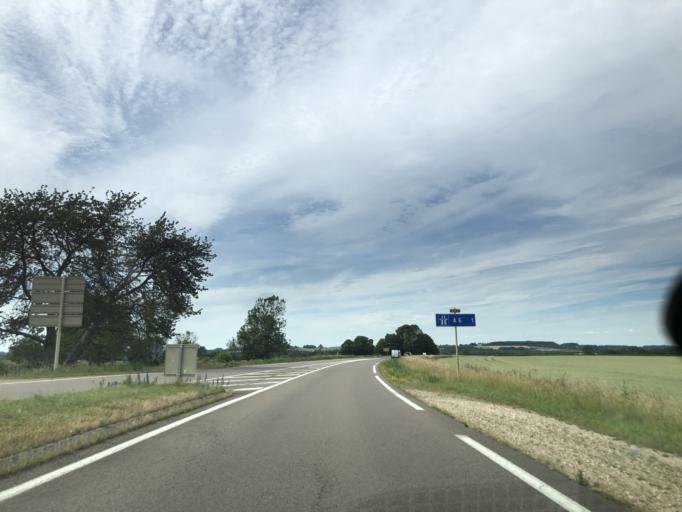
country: FR
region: Bourgogne
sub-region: Departement de l'Yonne
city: Avallon
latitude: 47.4871
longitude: 3.9902
